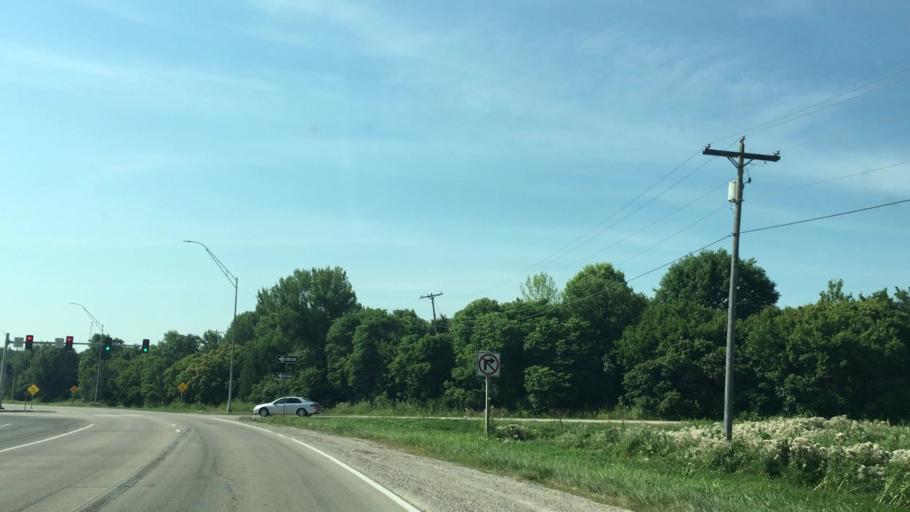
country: US
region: Iowa
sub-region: Johnson County
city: Iowa City
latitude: 41.6875
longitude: -91.5403
